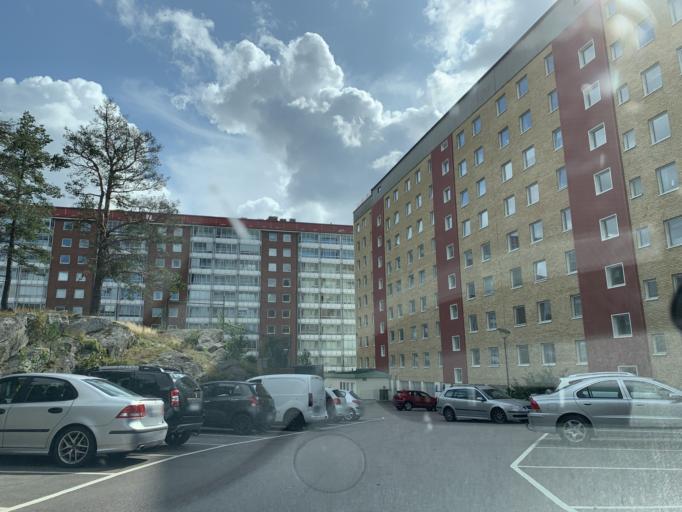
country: SE
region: Vaestra Goetaland
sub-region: Goteborg
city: Eriksbo
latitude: 57.7551
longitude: 12.0294
